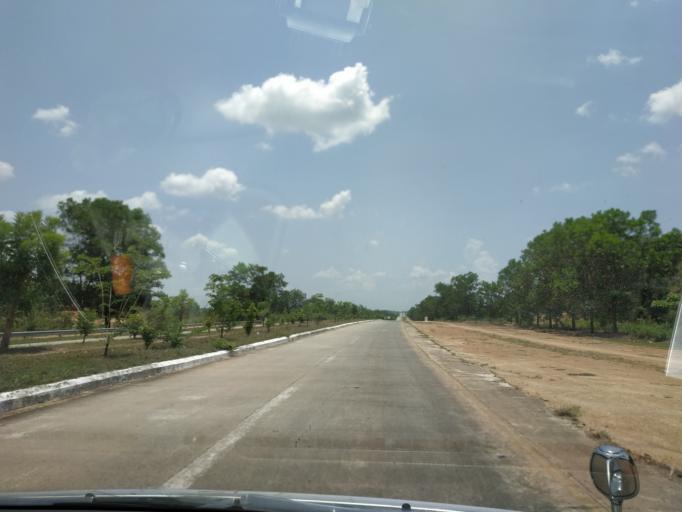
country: MM
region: Bago
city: Thanatpin
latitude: 17.3518
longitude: 96.2404
